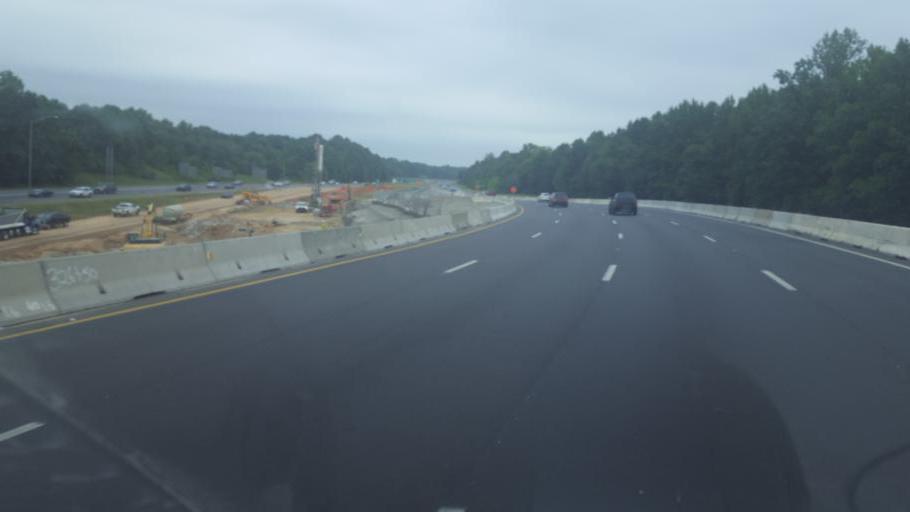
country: US
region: North Carolina
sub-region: Mecklenburg County
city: Charlotte
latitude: 35.2779
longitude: -80.8452
